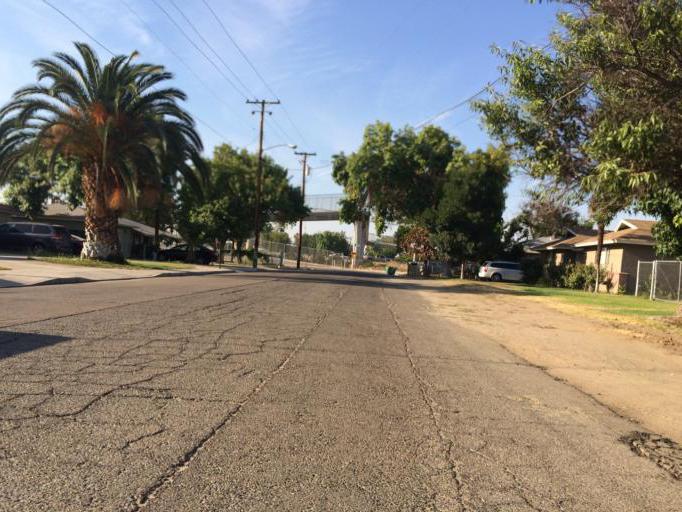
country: US
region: California
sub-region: Fresno County
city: Sunnyside
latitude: 36.7525
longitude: -119.7319
